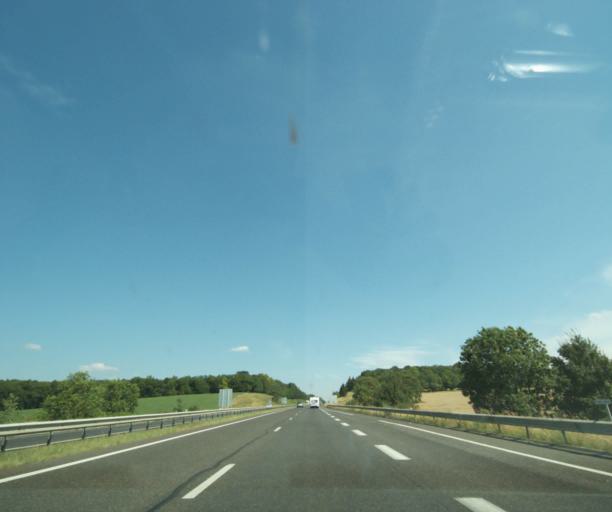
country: FR
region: Lorraine
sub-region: Departement de Meurthe-et-Moselle
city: Dommartin-les-Toul
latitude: 48.6342
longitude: 5.8818
